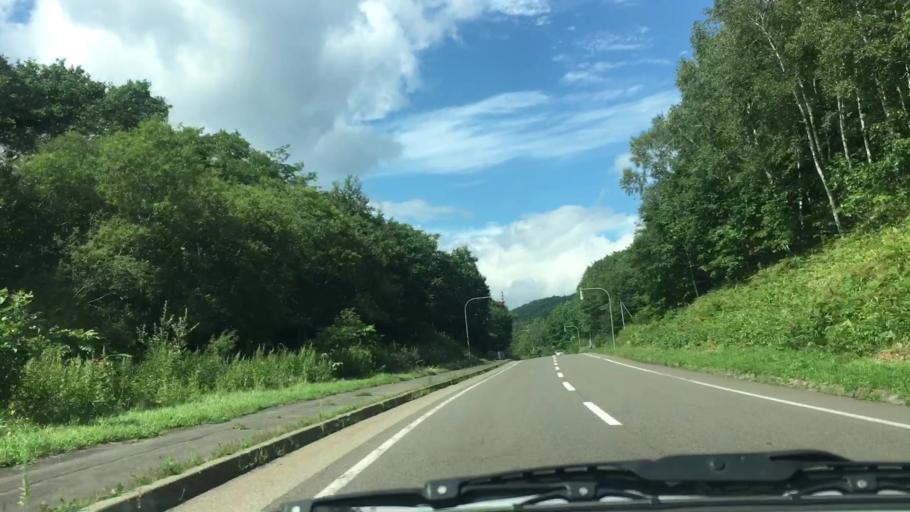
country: JP
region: Hokkaido
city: Otofuke
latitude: 43.3367
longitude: 143.2872
